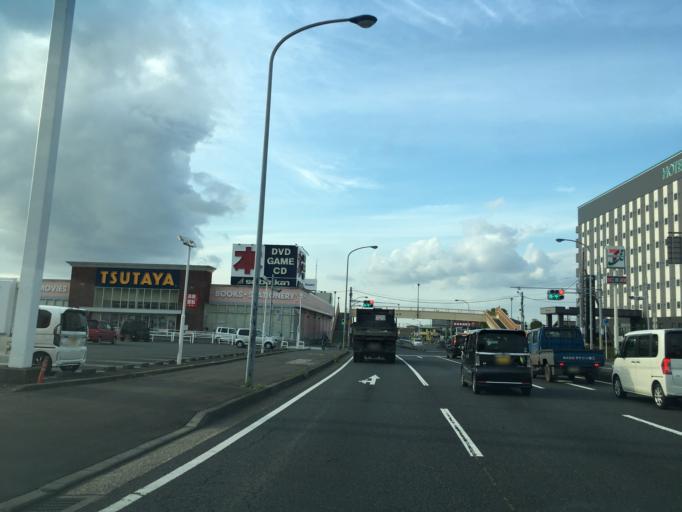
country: JP
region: Chiba
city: Kisarazu
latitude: 35.3810
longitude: 139.9424
